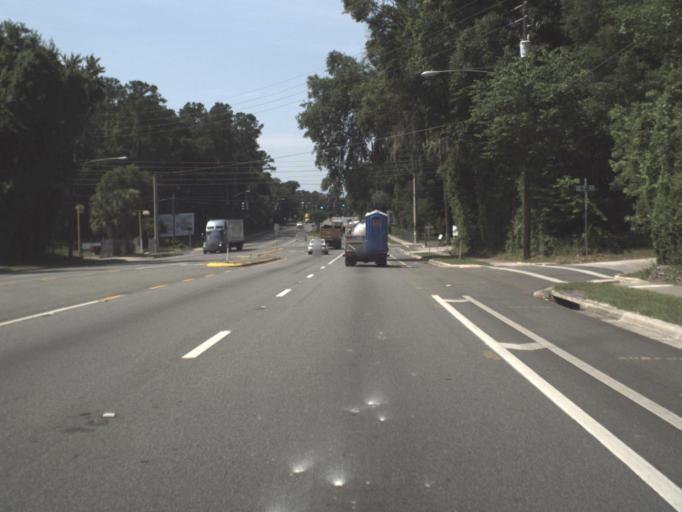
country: US
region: Florida
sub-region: Alachua County
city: Gainesville
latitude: 29.6495
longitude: -82.3116
